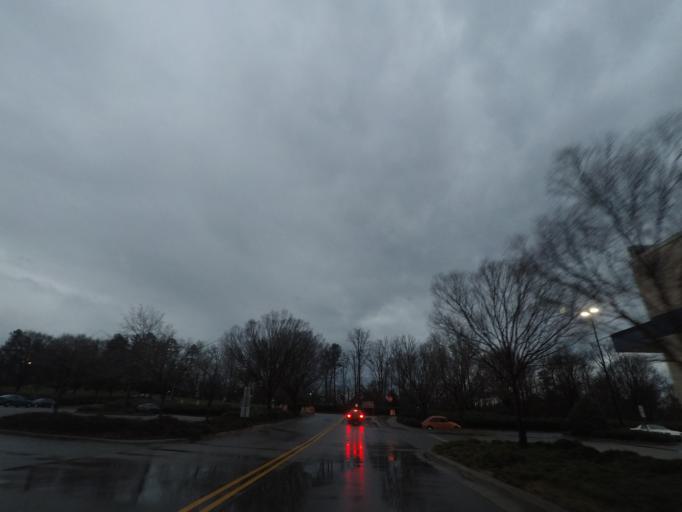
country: US
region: North Carolina
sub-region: Durham County
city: Durham
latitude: 35.9043
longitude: -78.9479
